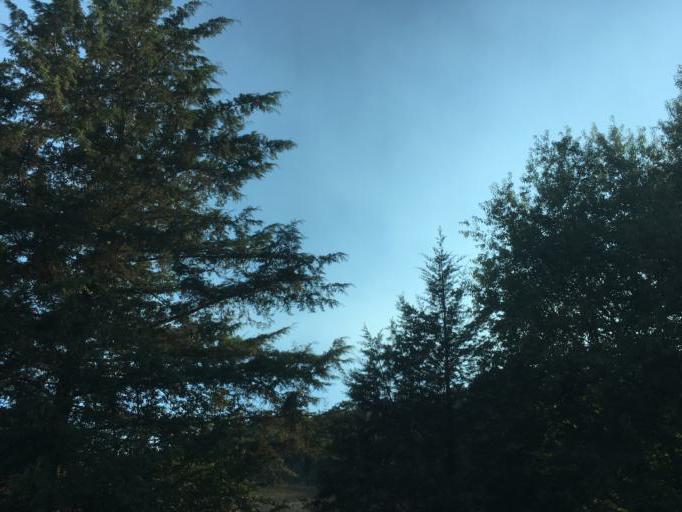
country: MX
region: Michoacan
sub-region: Morelia
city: Iratzio
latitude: 19.6216
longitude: -101.4621
